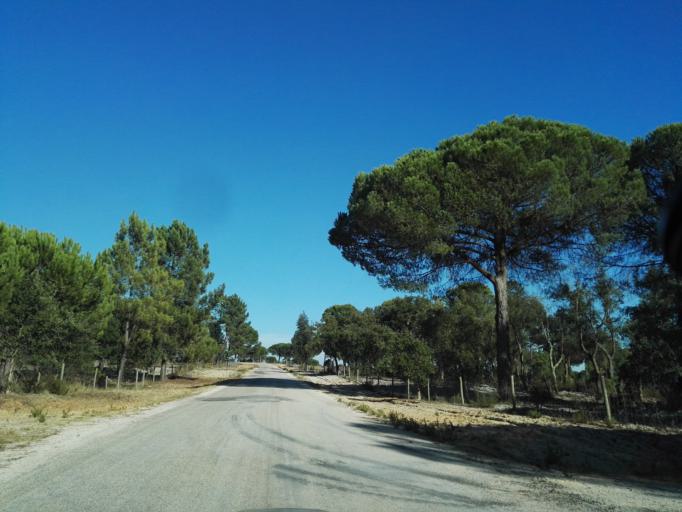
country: PT
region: Santarem
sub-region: Benavente
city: Poceirao
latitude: 38.8818
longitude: -8.7263
